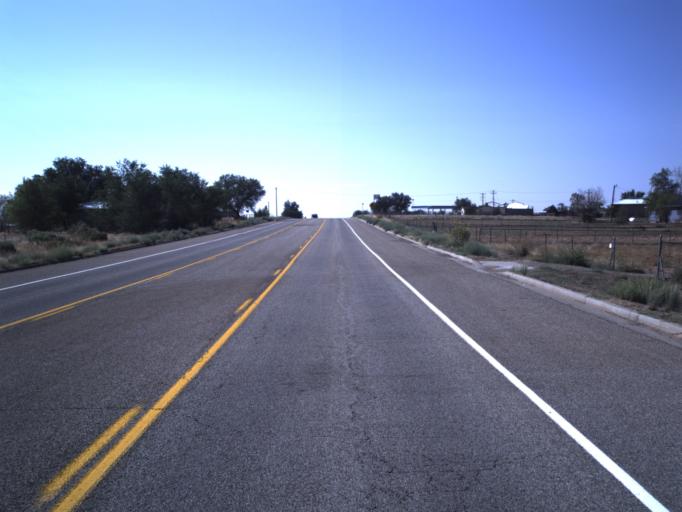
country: US
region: Utah
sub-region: San Juan County
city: Blanding
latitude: 37.4688
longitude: -109.4670
